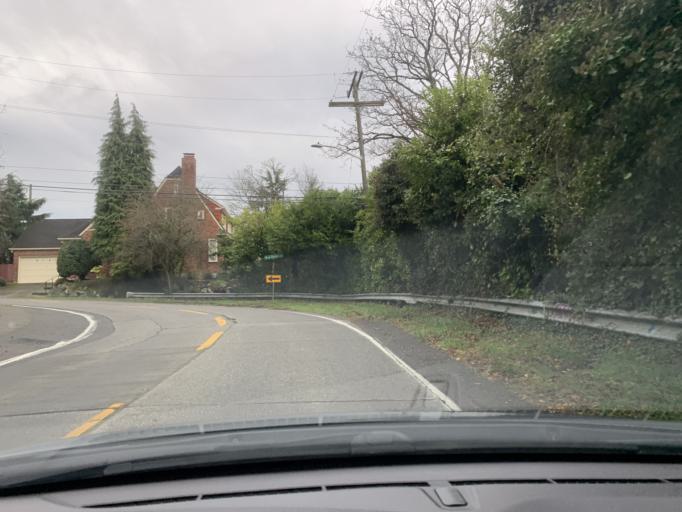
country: US
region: Washington
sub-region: King County
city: White Center
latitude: 47.5578
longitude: -122.3990
